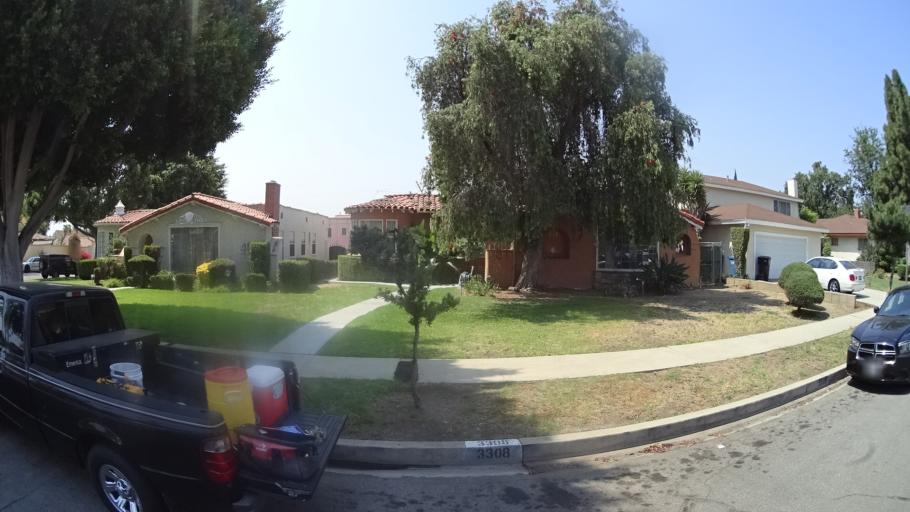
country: US
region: California
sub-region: Los Angeles County
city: Inglewood
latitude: 33.9645
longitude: -118.3290
